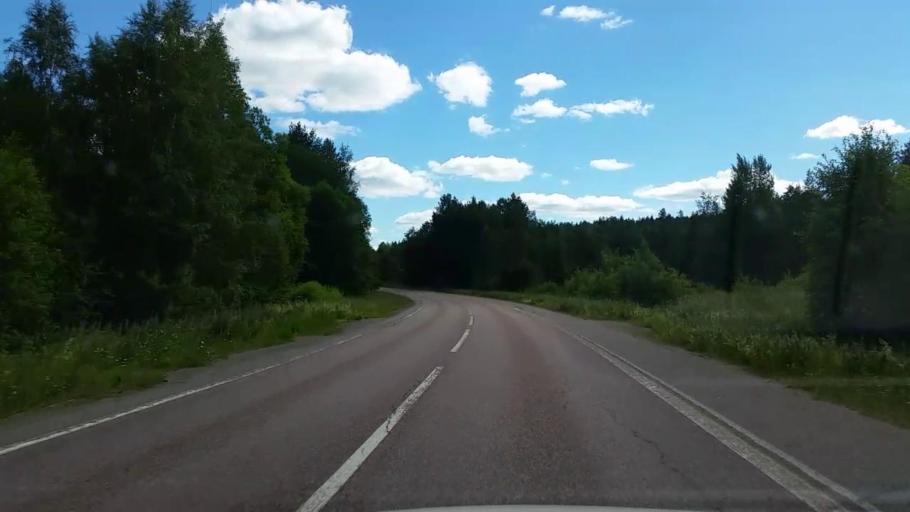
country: SE
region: Dalarna
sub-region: Faluns Kommun
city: Svardsjo
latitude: 60.8516
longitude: 15.7525
